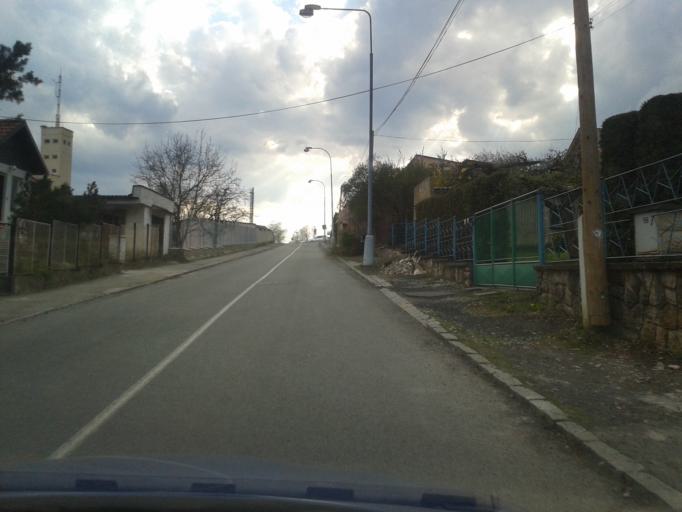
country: CZ
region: Central Bohemia
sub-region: Okres Beroun
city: Beroun
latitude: 49.9687
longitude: 14.0618
